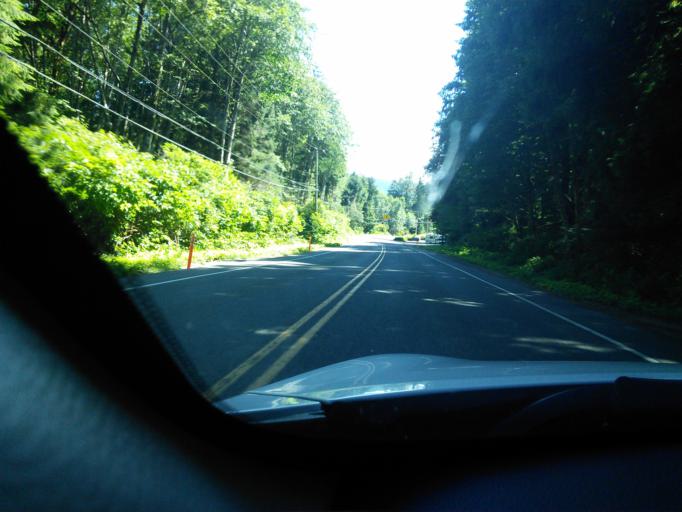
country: CA
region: British Columbia
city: Campbell River
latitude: 50.3237
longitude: -125.9222
